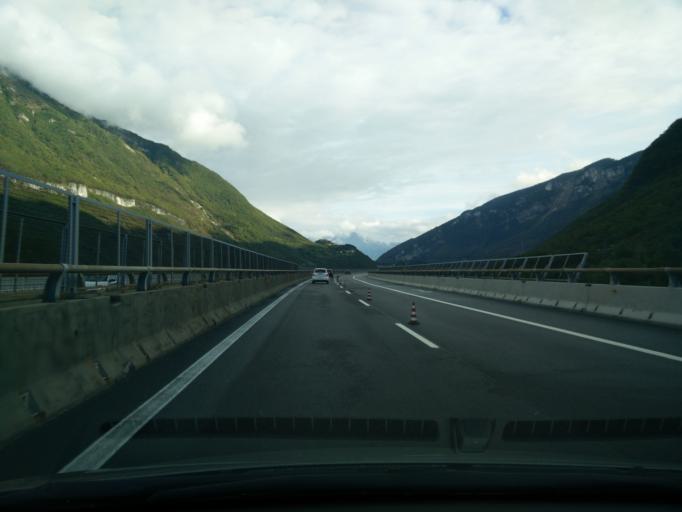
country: IT
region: Veneto
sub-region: Provincia di Treviso
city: Fregona
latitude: 46.0475
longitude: 12.3152
